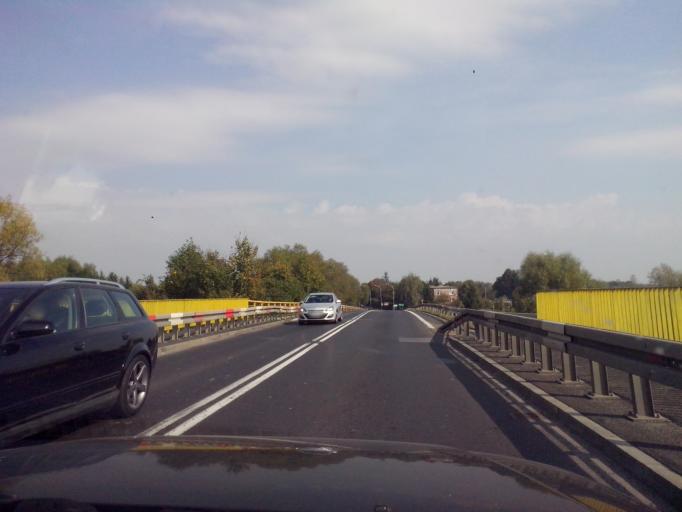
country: PL
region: Subcarpathian Voivodeship
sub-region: Powiat rzeszowski
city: Lutoryz
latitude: 49.9722
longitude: 21.9218
